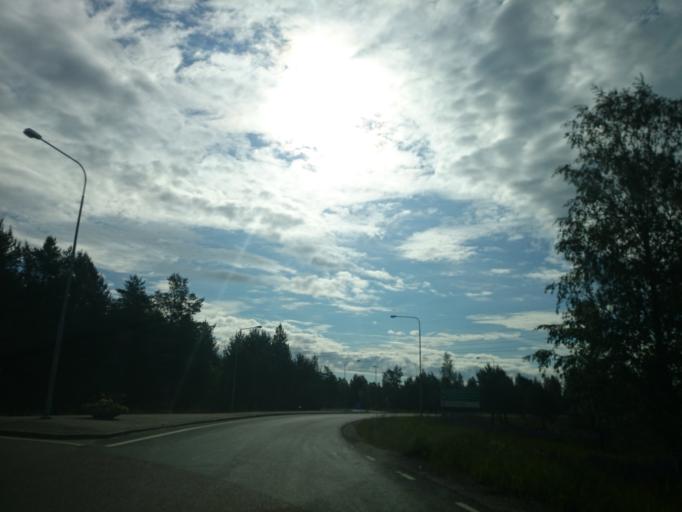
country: SE
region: Vaesternorrland
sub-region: Timra Kommun
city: Timra
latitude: 62.4979
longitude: 17.3339
